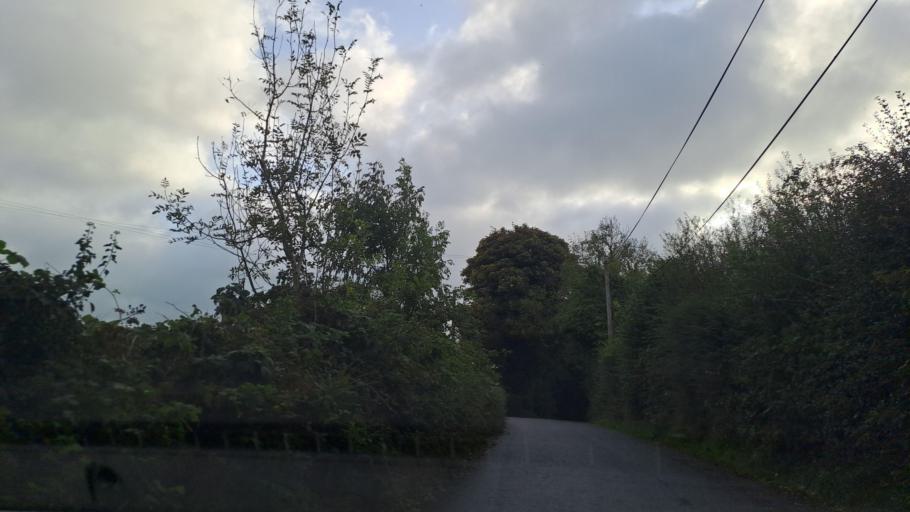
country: IE
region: Ulster
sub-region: An Cabhan
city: Kingscourt
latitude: 53.9559
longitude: -6.7915
